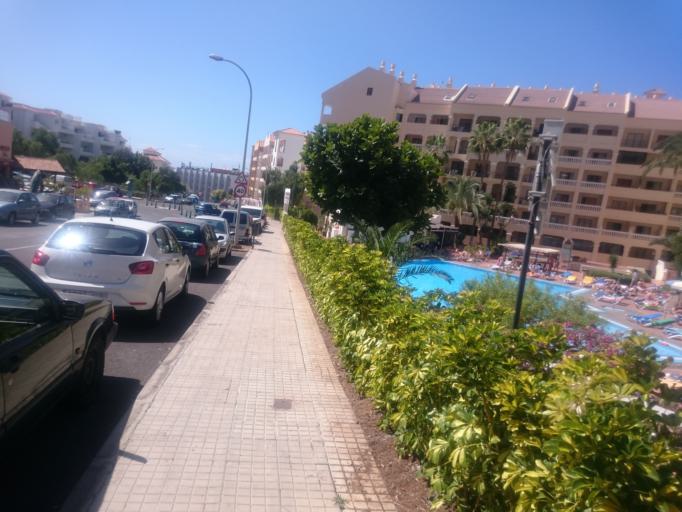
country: ES
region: Canary Islands
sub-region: Provincia de Santa Cruz de Tenerife
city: Playa de las Americas
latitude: 28.0552
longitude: -16.7038
